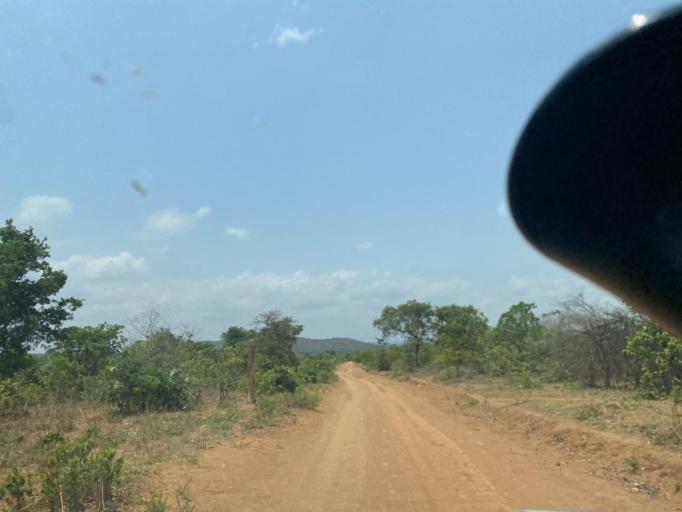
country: ZM
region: Lusaka
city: Chongwe
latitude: -15.5168
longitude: 28.8803
